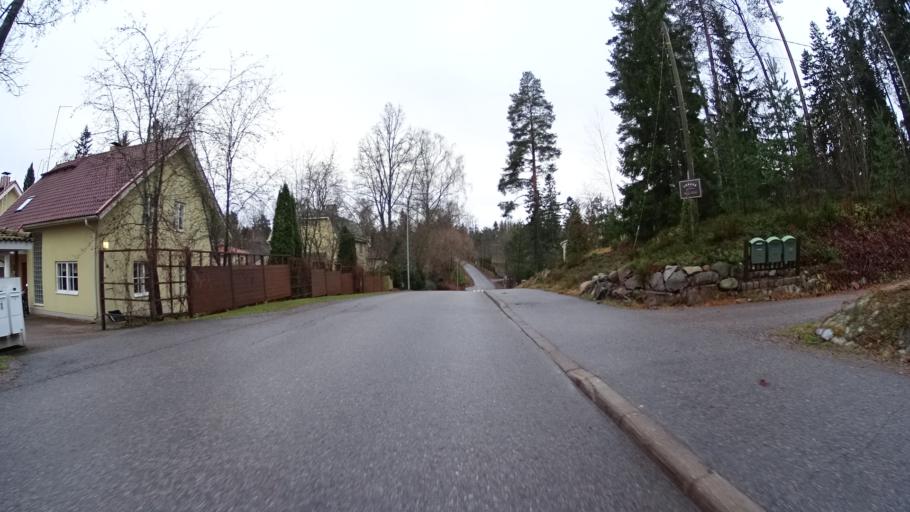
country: FI
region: Uusimaa
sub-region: Helsinki
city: Kauniainen
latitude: 60.2192
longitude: 24.7365
